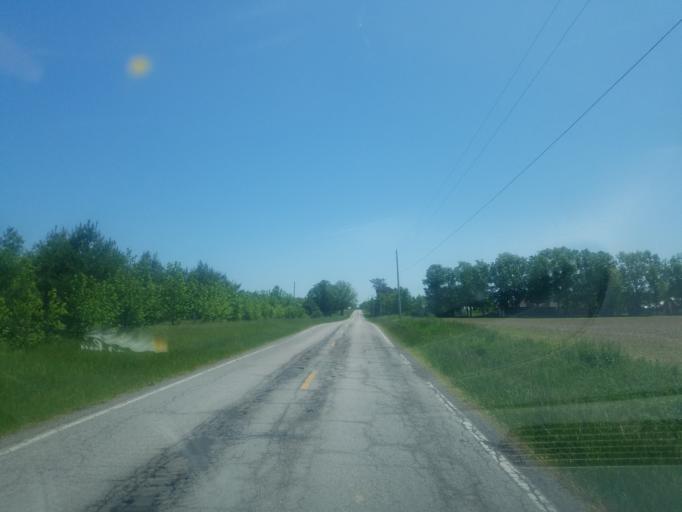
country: US
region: Ohio
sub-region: Huron County
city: Wakeman
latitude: 41.1965
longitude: -82.3887
